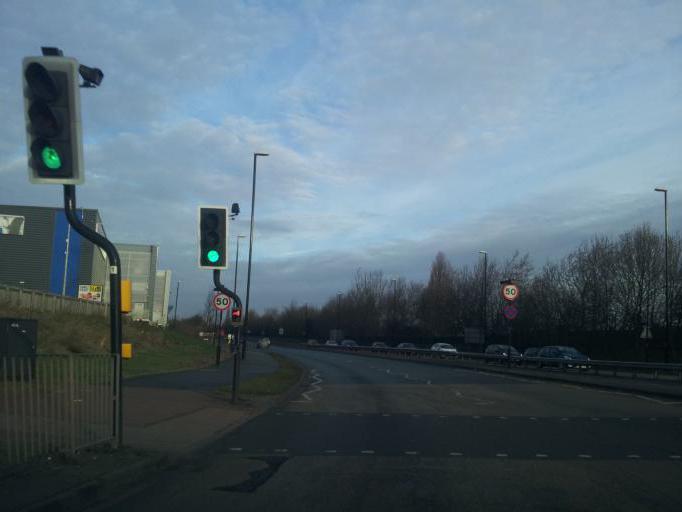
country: GB
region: England
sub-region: Warwickshire
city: Exhall
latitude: 52.4306
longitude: -1.4864
